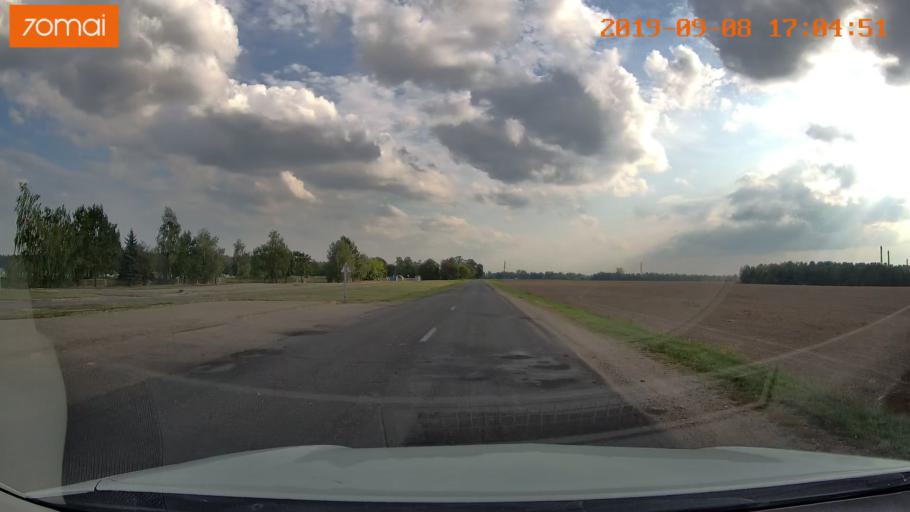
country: BY
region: Grodnenskaya
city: Hrodna
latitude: 53.6854
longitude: 23.9556
